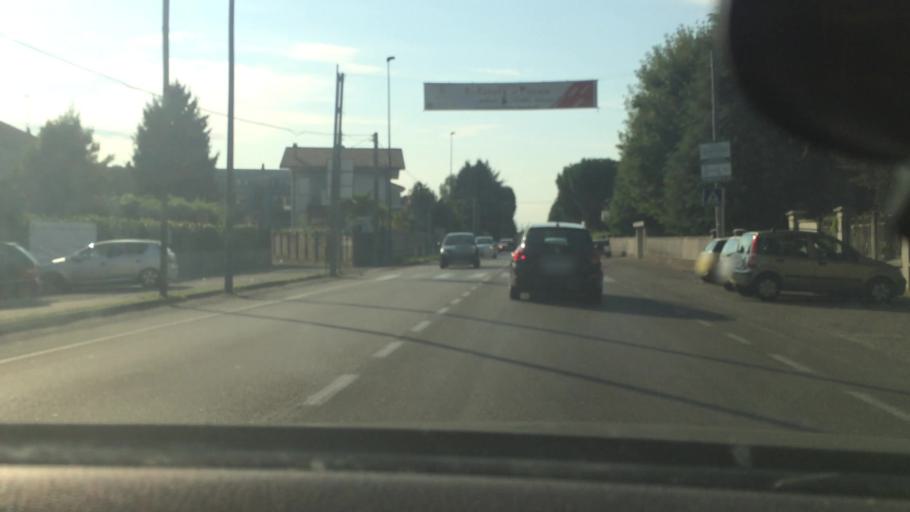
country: IT
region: Lombardy
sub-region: Provincia di Varese
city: Gerenzano
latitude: 45.6390
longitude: 9.0064
